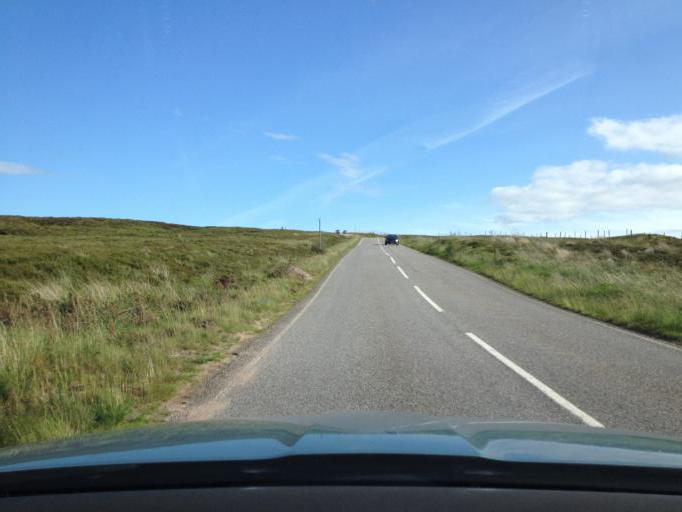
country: GB
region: Scotland
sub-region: Aberdeenshire
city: Laurencekirk
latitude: 56.9203
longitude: -2.5796
